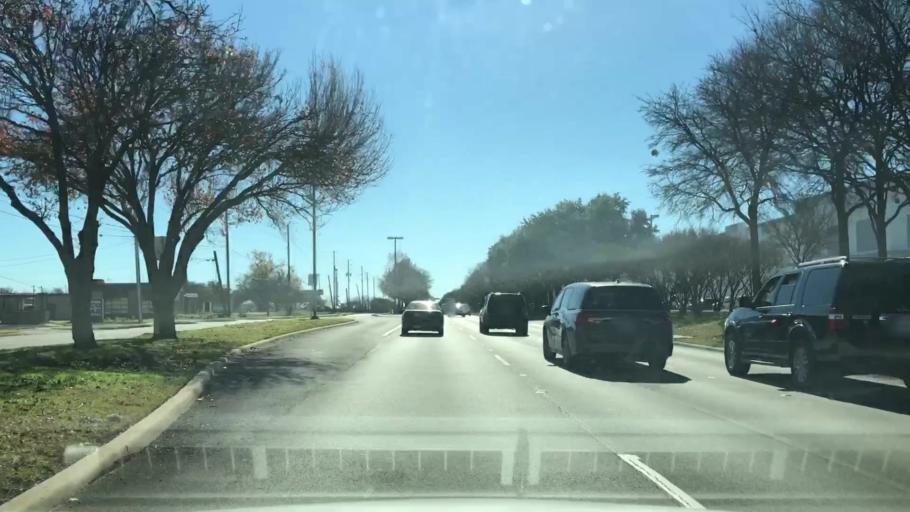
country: US
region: Texas
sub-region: Dallas County
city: Coppell
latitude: 32.9470
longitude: -96.9936
